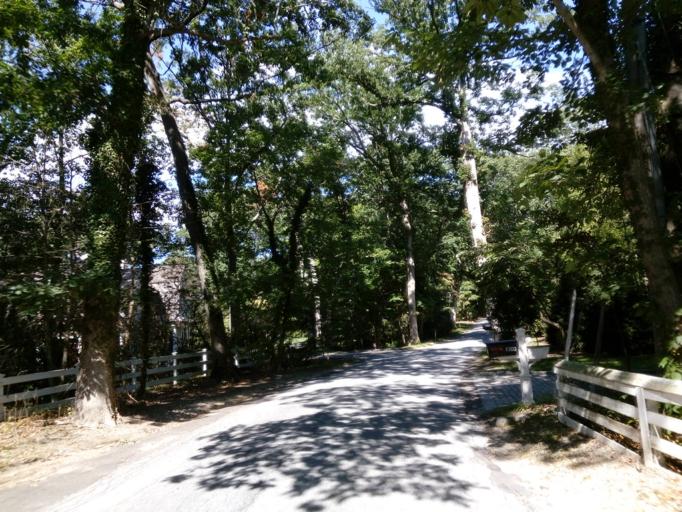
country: US
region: New York
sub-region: Nassau County
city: Laurel Hollow
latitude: 40.8656
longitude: -73.4772
